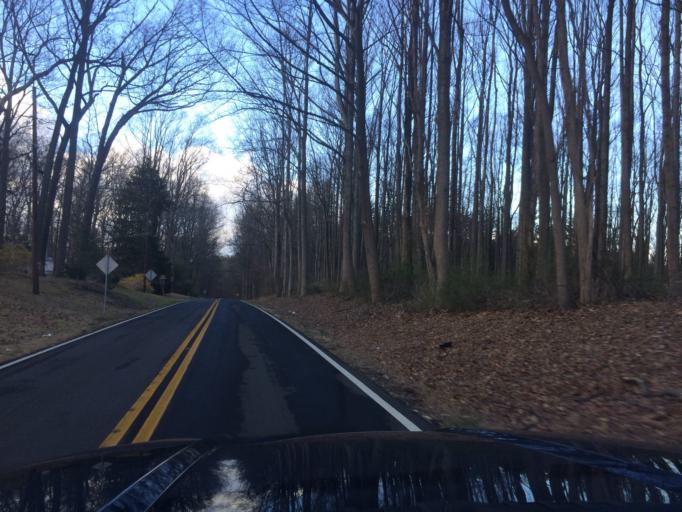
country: US
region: Maryland
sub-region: Carroll County
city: Eldersburg
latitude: 39.3848
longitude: -76.9077
